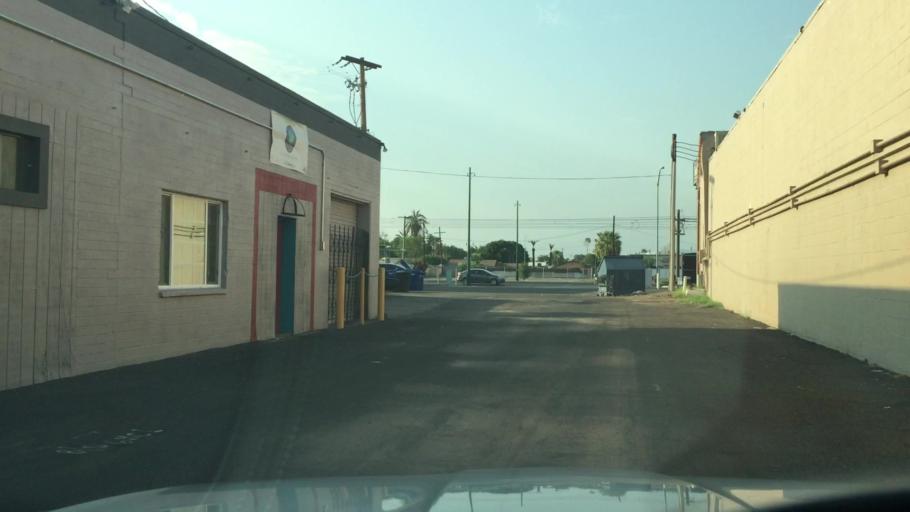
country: US
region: Arizona
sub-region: Maricopa County
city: Mesa
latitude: 33.4142
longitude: -111.8407
